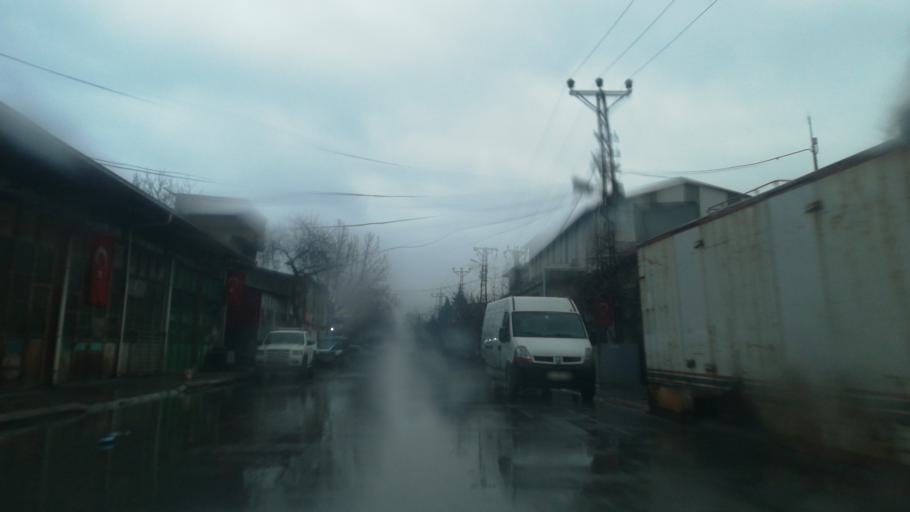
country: TR
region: Kahramanmaras
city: Kahramanmaras
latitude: 37.5600
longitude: 36.9609
